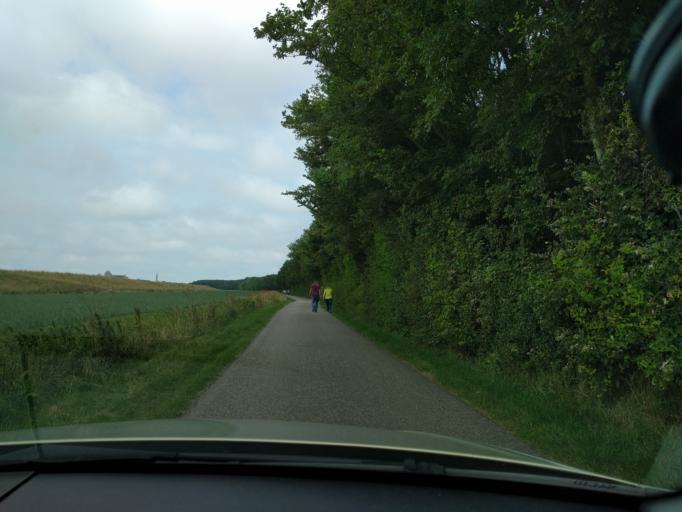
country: NL
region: Zeeland
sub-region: Gemeente Veere
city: Veere
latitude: 51.5349
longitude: 3.6780
